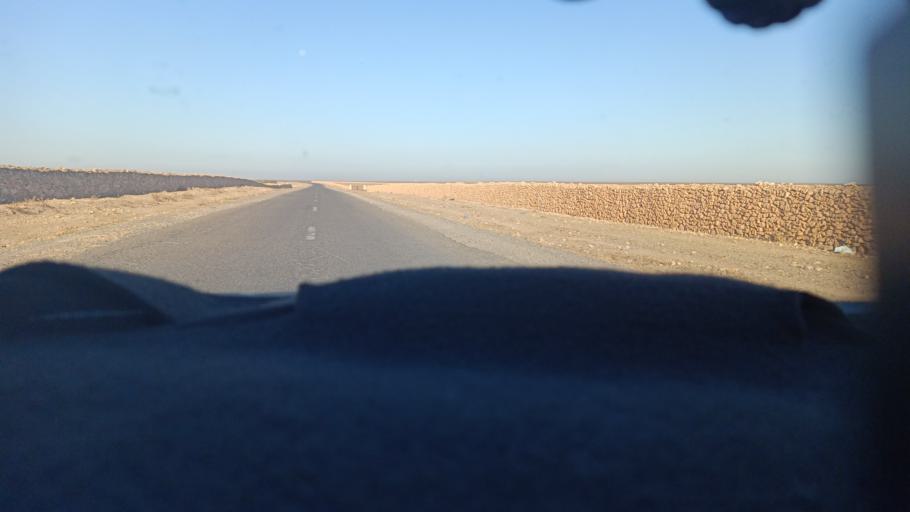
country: MA
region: Doukkala-Abda
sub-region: Safi
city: Youssoufia
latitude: 32.3716
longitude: -8.6937
